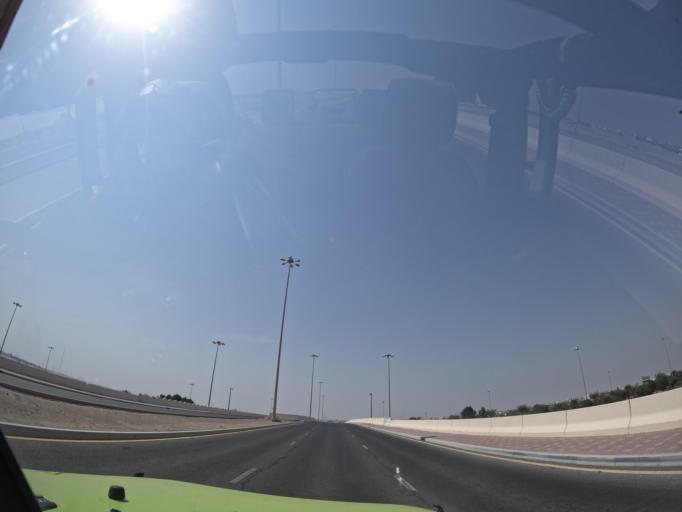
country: AE
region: Abu Dhabi
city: Abu Dhabi
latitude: 24.3397
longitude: 54.6376
